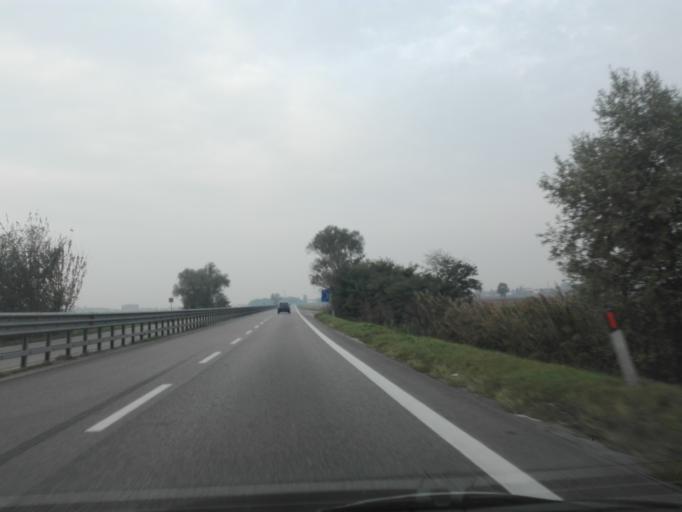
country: IT
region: Veneto
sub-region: Provincia di Rovigo
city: San Bellino
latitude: 45.0241
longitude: 11.6042
